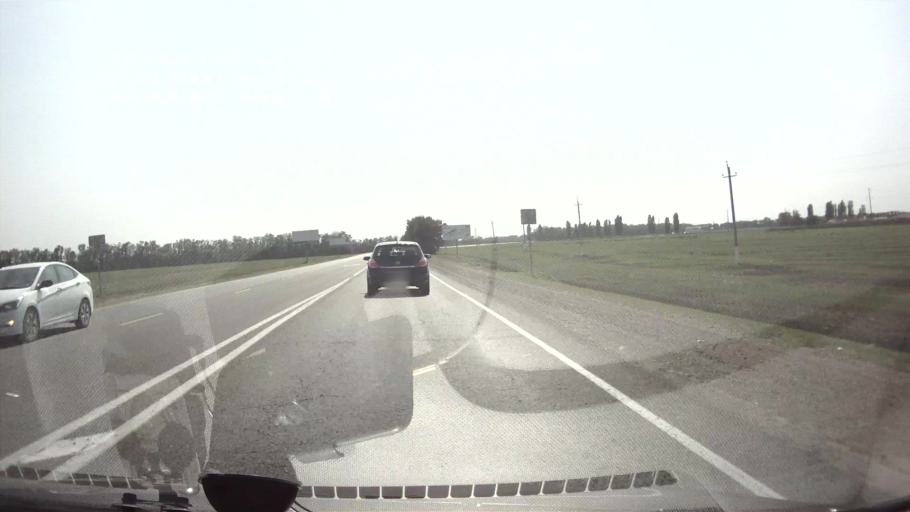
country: RU
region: Krasnodarskiy
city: Vasyurinskaya
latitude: 45.1027
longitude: 39.3871
